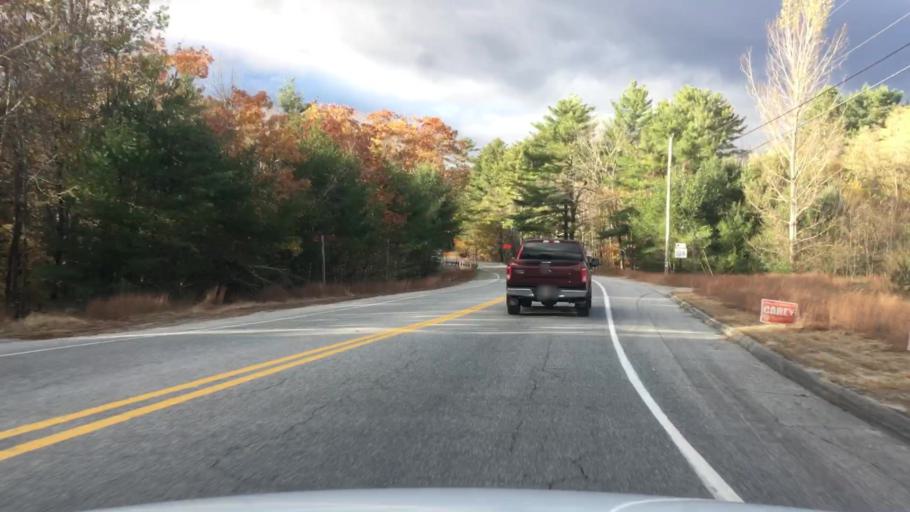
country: US
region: Maine
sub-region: Androscoggin County
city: Livermore
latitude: 44.3780
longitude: -70.2501
